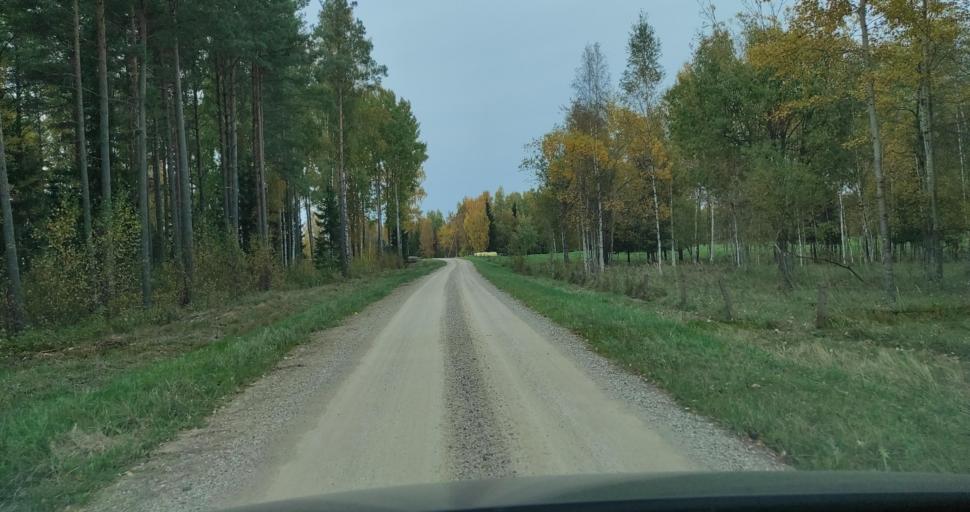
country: LV
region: Kuldigas Rajons
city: Kuldiga
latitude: 57.0249
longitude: 22.1995
